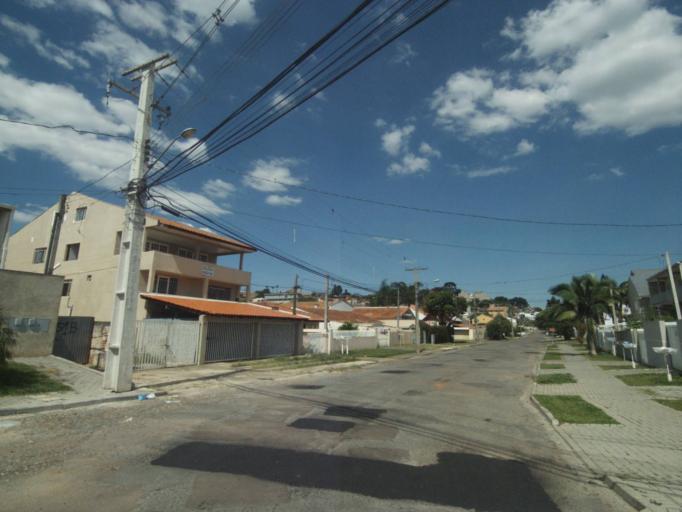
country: BR
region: Parana
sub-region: Curitiba
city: Curitiba
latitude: -25.4733
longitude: -49.2420
